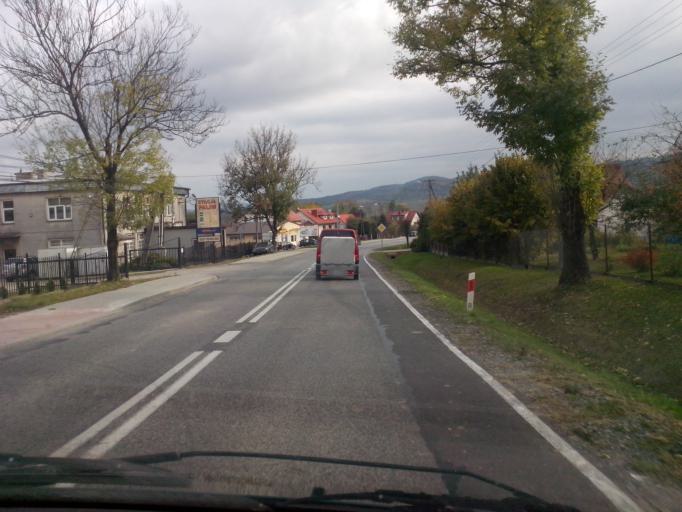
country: PL
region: Subcarpathian Voivodeship
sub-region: Powiat strzyzowski
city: Wisniowa
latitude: 49.8720
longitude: 21.6588
